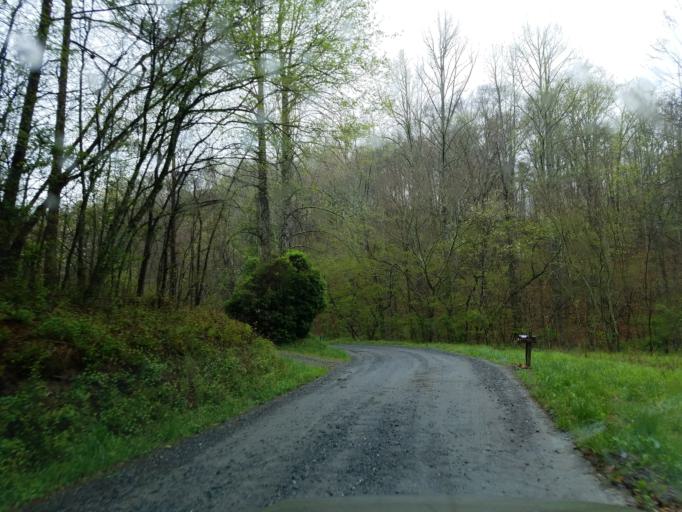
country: US
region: Georgia
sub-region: Fannin County
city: Blue Ridge
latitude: 34.8546
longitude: -84.2301
